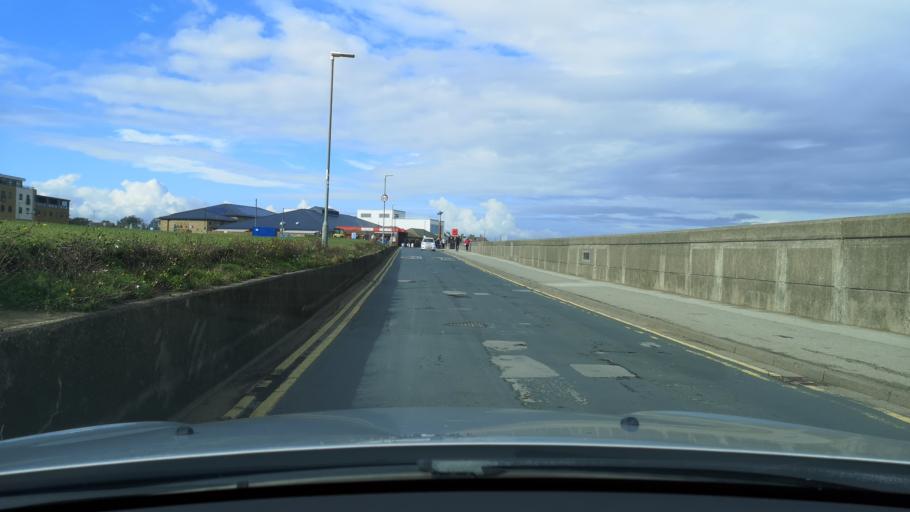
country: GB
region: England
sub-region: East Riding of Yorkshire
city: Hornsea
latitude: 53.9109
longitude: -0.1596
